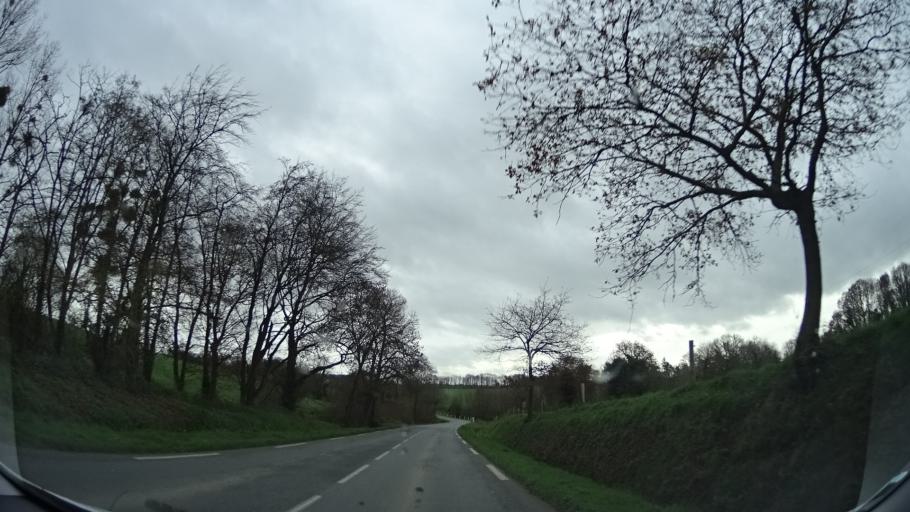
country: FR
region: Brittany
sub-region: Departement des Cotes-d'Armor
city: Les Champs-Geraux
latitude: 48.4200
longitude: -2.0017
